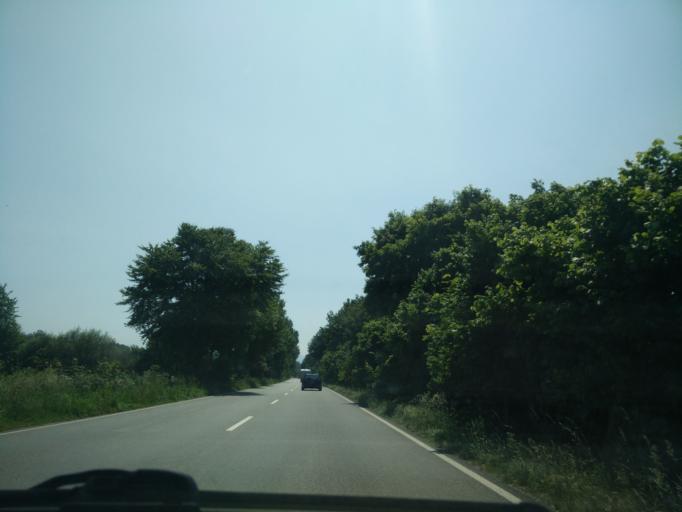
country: DE
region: Bavaria
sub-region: Upper Bavaria
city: Laufen
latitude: 47.8987
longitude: 12.9515
